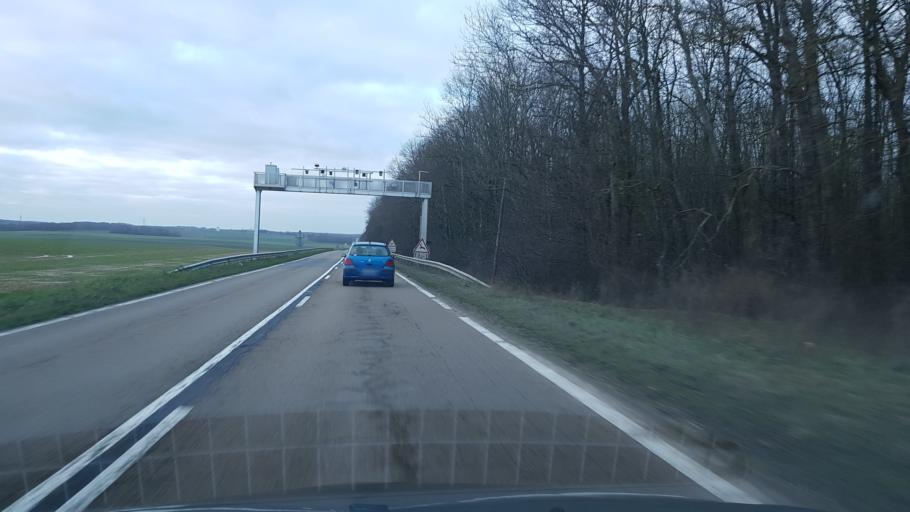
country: FR
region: Champagne-Ardenne
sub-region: Departement de la Marne
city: Esternay
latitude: 48.7200
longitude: 3.5369
